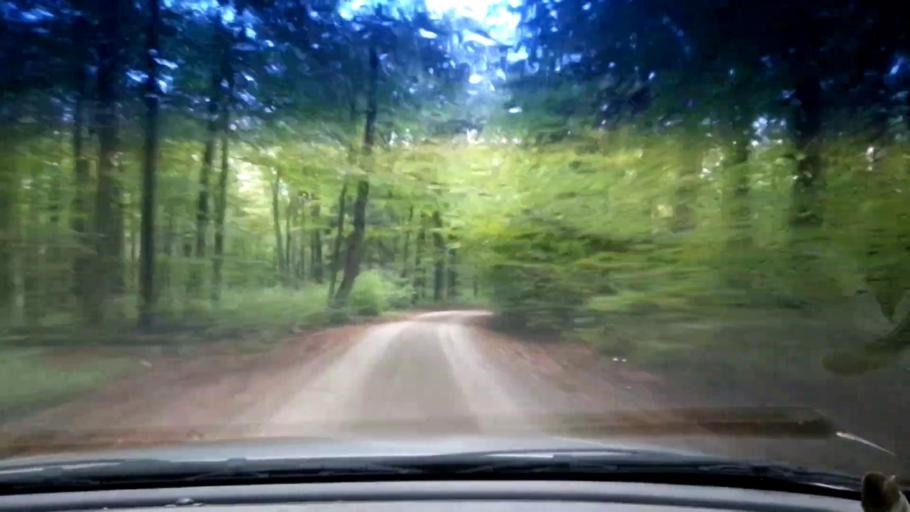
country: DE
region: Bavaria
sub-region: Upper Franconia
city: Burgwindheim
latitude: 49.8416
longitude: 10.6371
